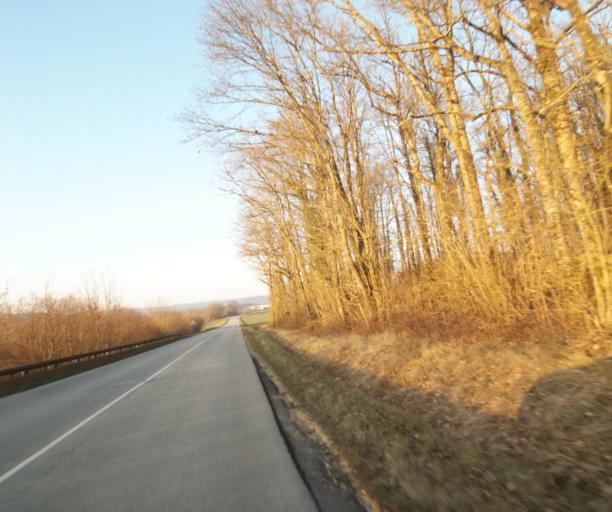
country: FR
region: Champagne-Ardenne
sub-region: Departement de la Haute-Marne
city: Bienville
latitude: 48.5907
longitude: 5.0422
